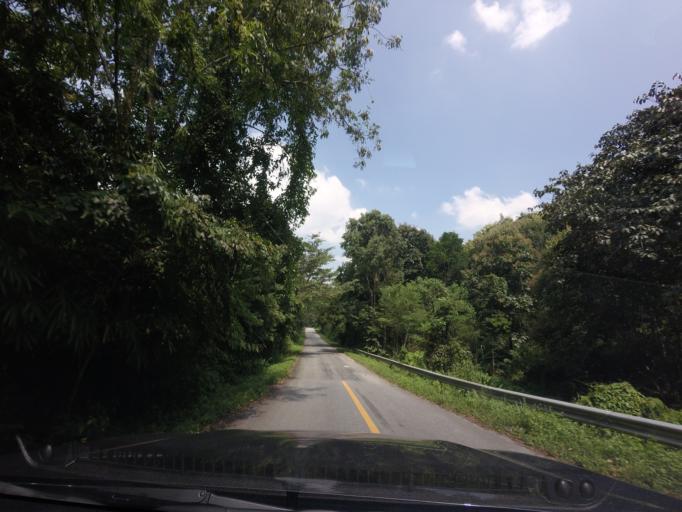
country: TH
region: Loei
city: Na Haeo
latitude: 17.6262
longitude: 100.9050
